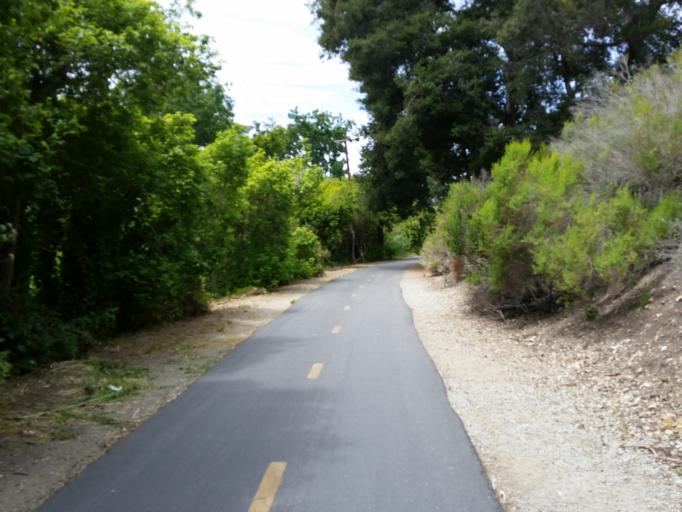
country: US
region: California
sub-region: San Luis Obispo County
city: Avila Beach
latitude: 35.1846
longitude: -120.7051
